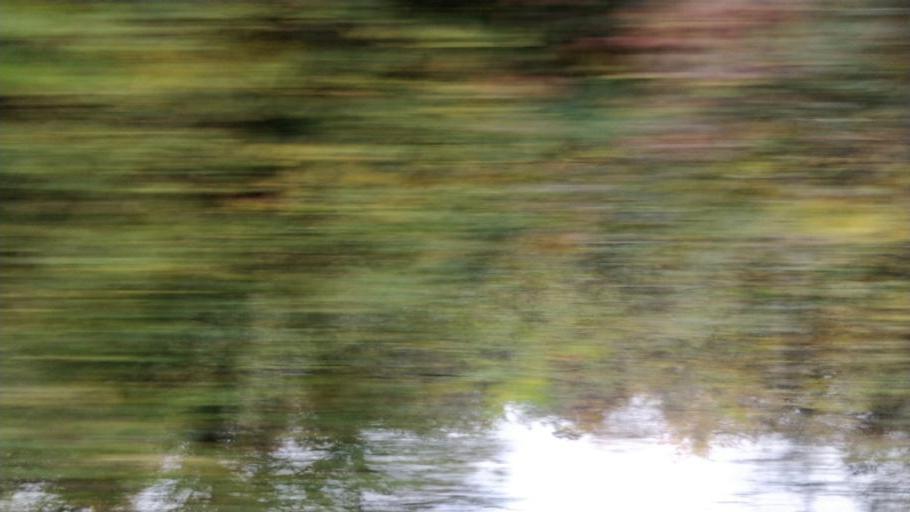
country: GB
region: England
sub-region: Borough of Wigan
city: Ince-in-Makerfield
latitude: 53.5399
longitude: -2.6183
